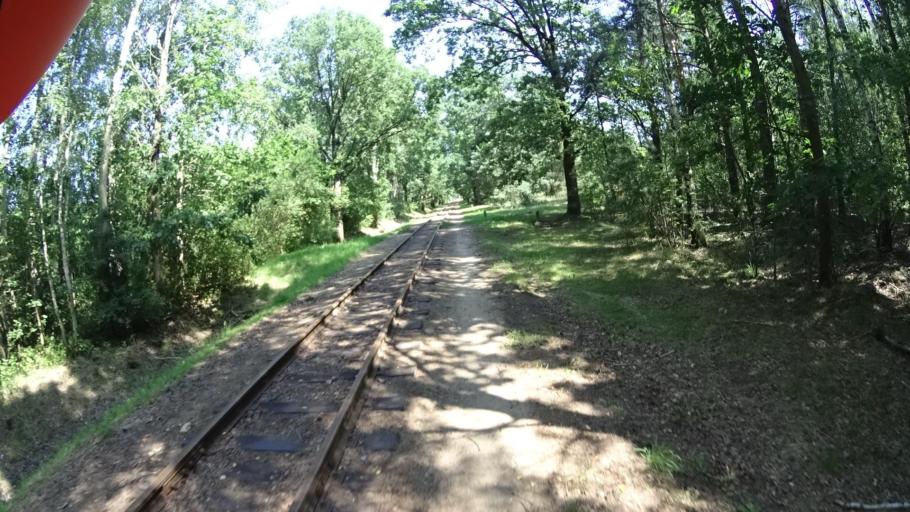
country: PL
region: Masovian Voivodeship
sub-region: Powiat piaseczynski
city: Tarczyn
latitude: 51.9893
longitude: 20.8867
